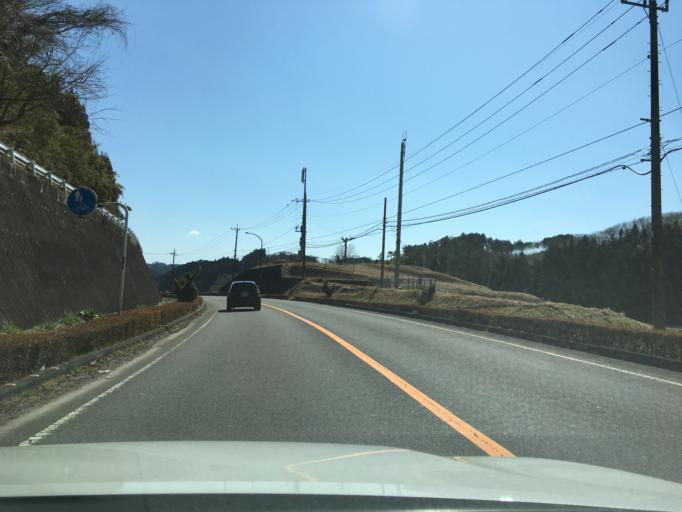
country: JP
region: Tochigi
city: Kuroiso
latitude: 37.0319
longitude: 140.1732
